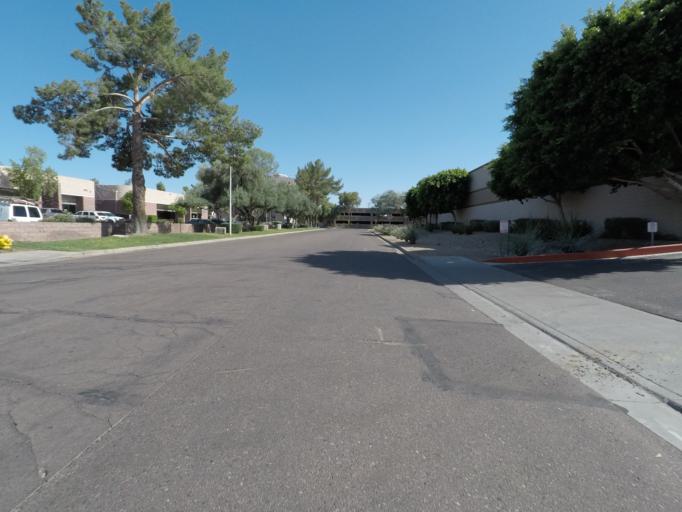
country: US
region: Arizona
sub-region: Maricopa County
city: Tempe Junction
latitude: 33.4146
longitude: -111.9747
